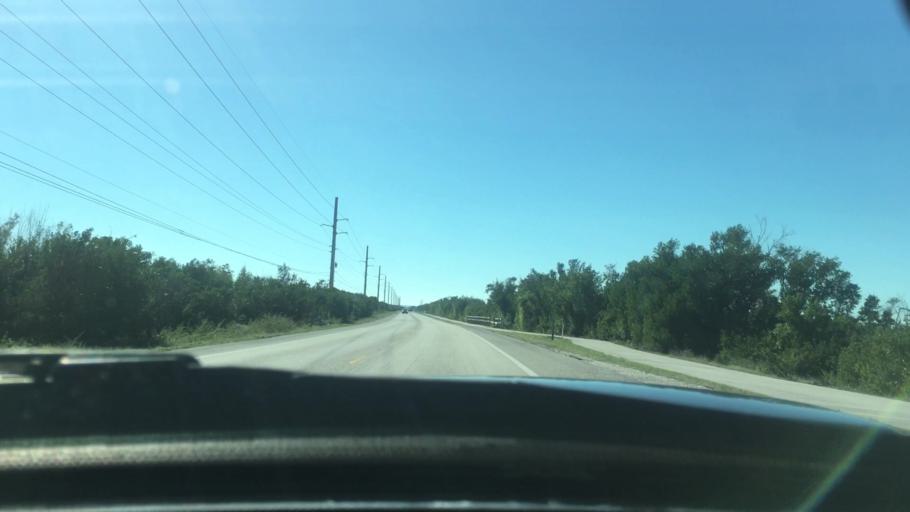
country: US
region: Florida
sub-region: Monroe County
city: Big Pine Key
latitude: 24.6690
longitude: -81.2533
